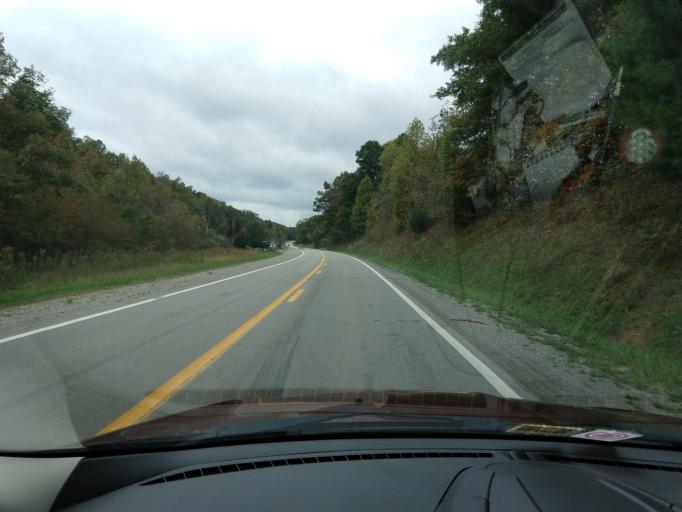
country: US
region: West Virginia
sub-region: Barbour County
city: Belington
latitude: 39.0444
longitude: -79.9565
